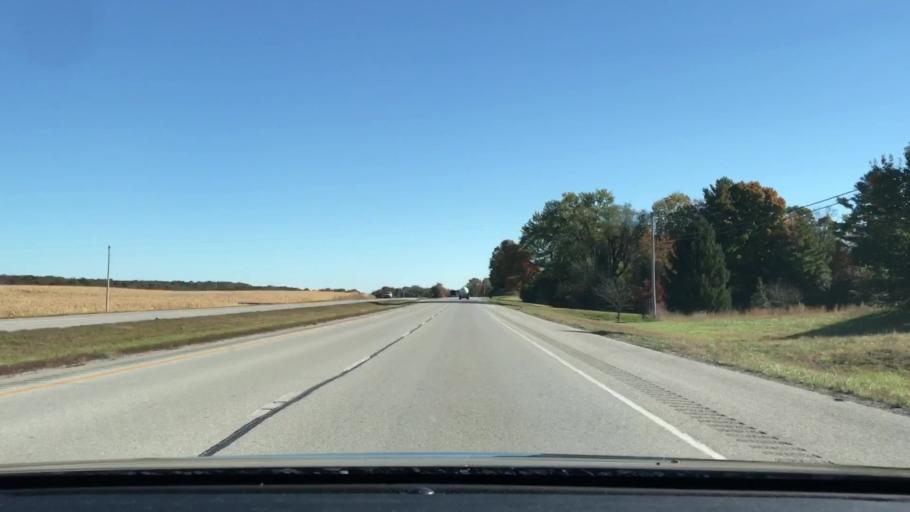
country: US
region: Kentucky
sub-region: Warren County
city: Bowling Green
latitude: 36.9171
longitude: -86.5637
